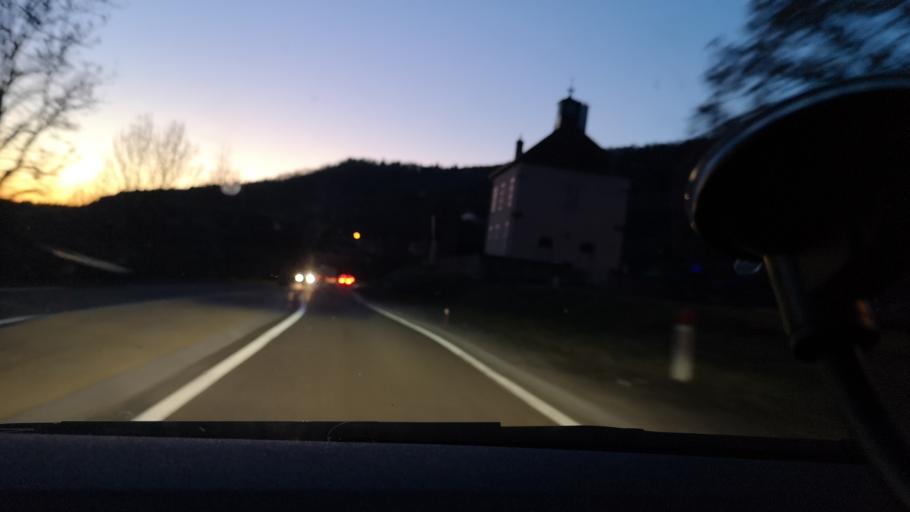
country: FR
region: Franche-Comte
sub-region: Departement du Jura
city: Champagnole
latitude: 46.7585
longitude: 5.9400
